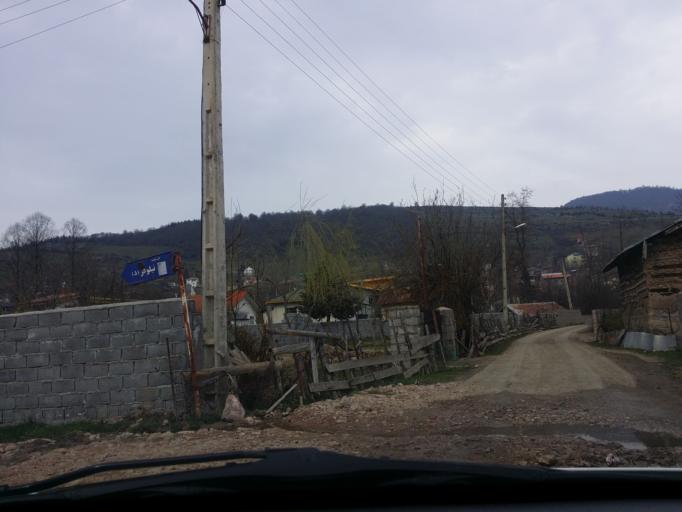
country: IR
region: Mazandaran
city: `Abbasabad
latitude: 36.5459
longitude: 51.1656
